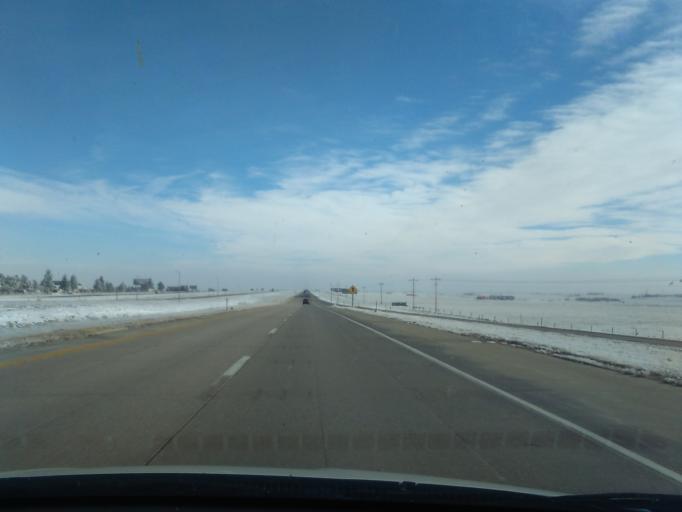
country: US
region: Wyoming
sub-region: Laramie County
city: Fox Farm-College
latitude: 41.1579
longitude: -104.5200
